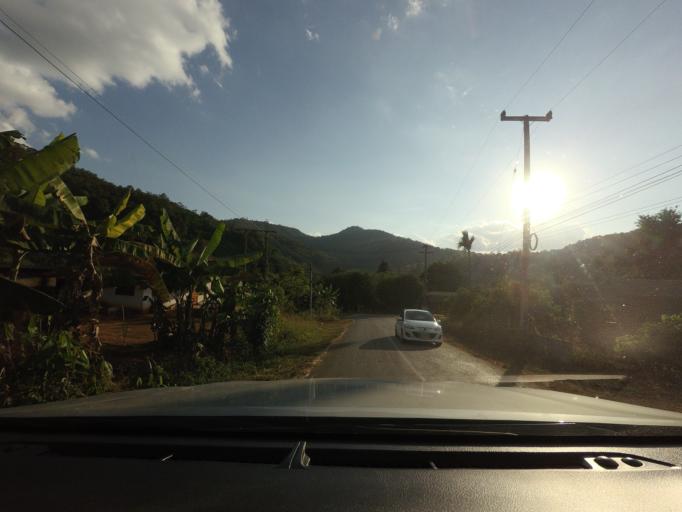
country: TH
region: Chiang Mai
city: Phrao
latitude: 19.4956
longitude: 99.1665
